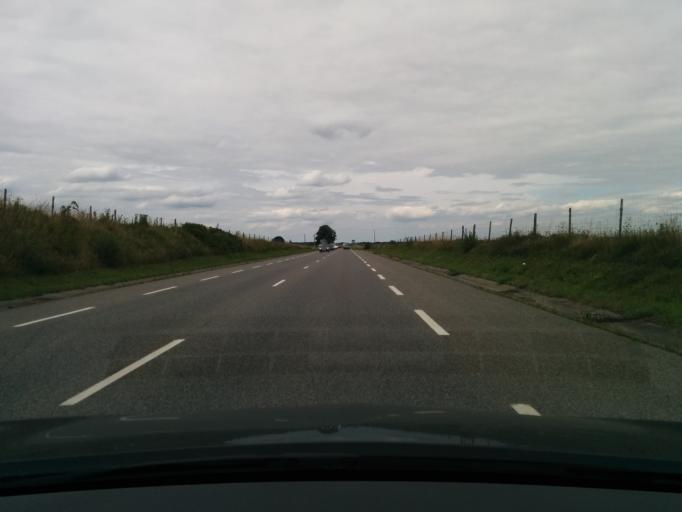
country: FR
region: Midi-Pyrenees
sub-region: Departement des Hautes-Pyrenees
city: La Barthe-de-Neste
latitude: 43.0449
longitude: 0.3631
